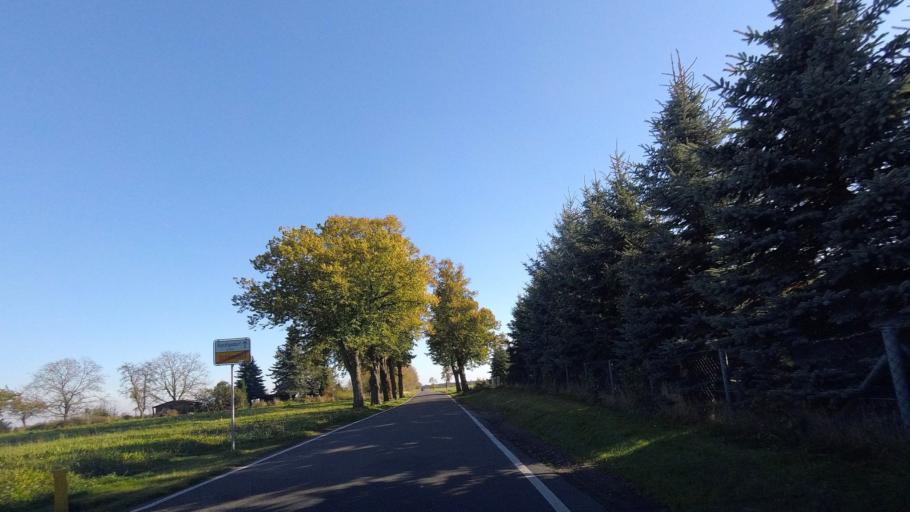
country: DE
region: Saxony-Anhalt
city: Zahna
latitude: 51.9771
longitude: 12.8325
